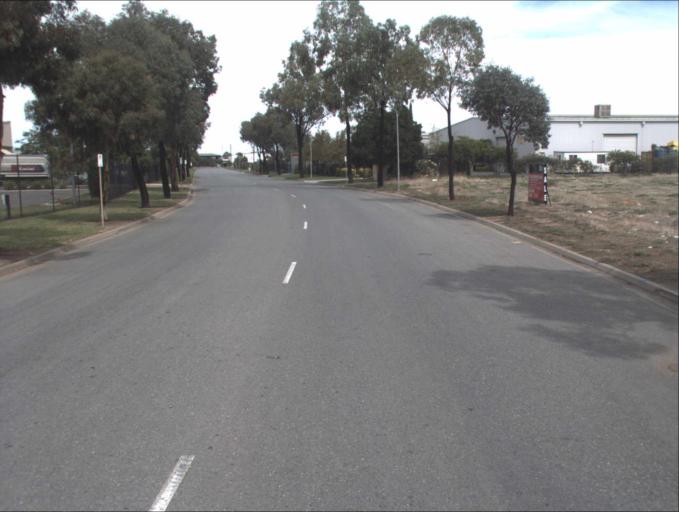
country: AU
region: South Australia
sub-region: Port Adelaide Enfield
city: Blair Athol
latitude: -34.8429
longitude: 138.5700
